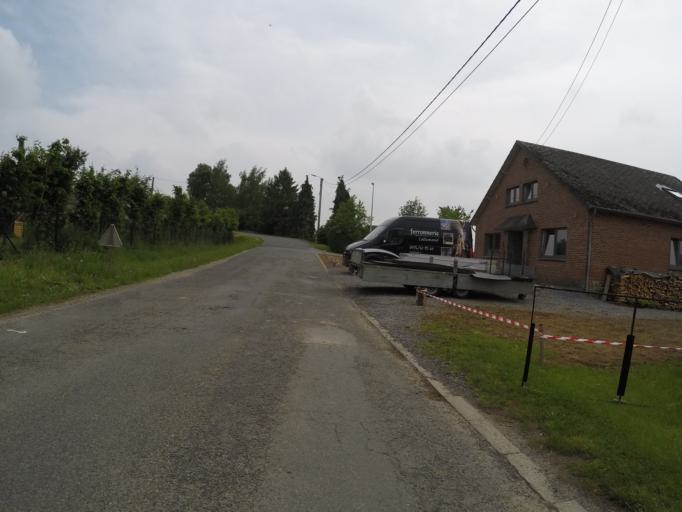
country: BE
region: Wallonia
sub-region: Province de Namur
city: Assesse
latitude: 50.3337
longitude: 5.0623
